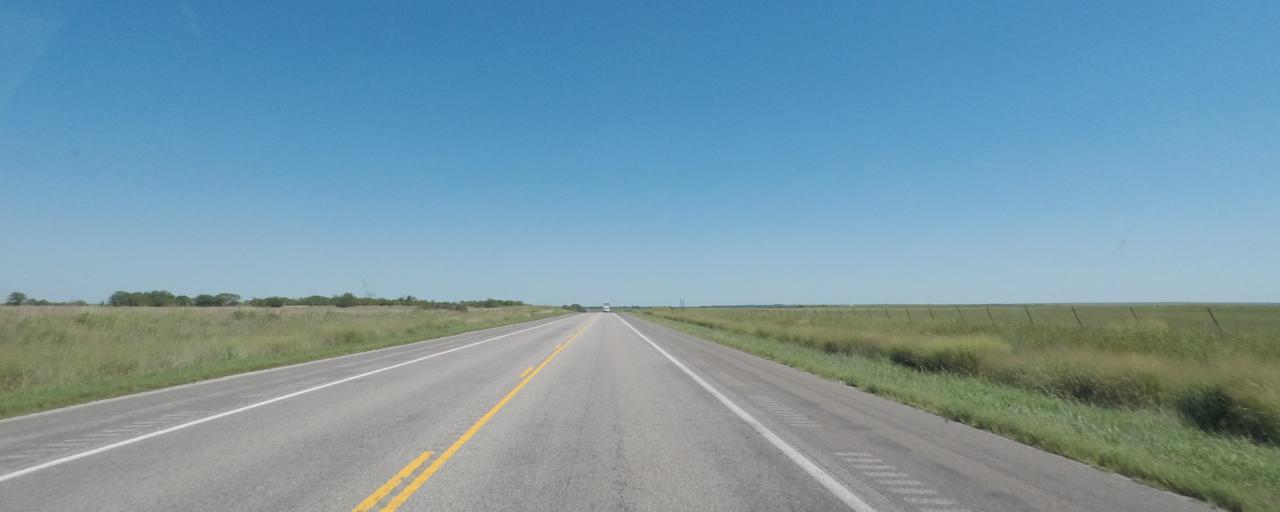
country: US
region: Kansas
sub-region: Chase County
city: Cottonwood Falls
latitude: 38.4056
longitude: -96.4722
